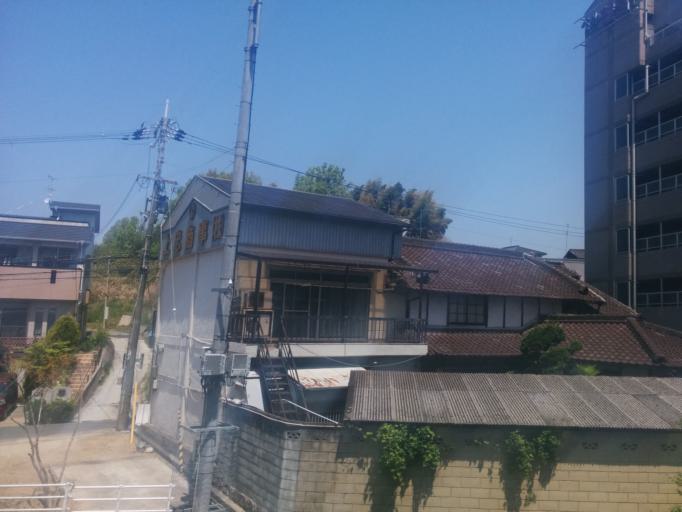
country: JP
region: Osaka
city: Kashihara
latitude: 34.5541
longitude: 135.6703
